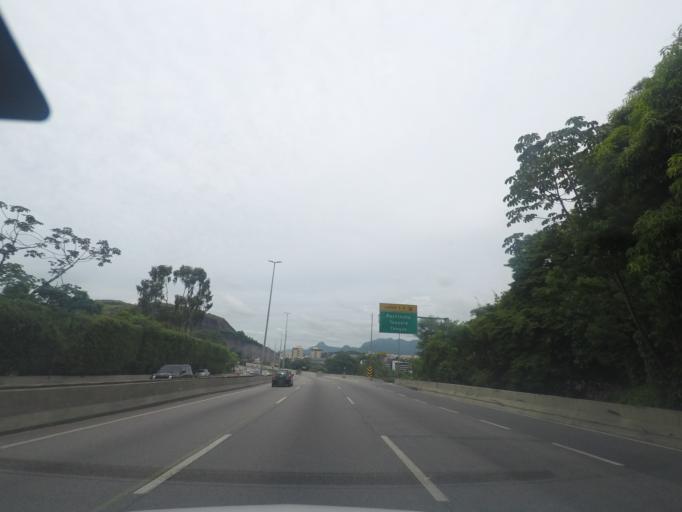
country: BR
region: Rio de Janeiro
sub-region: Sao Joao De Meriti
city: Sao Joao de Meriti
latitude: -22.9257
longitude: -43.3397
